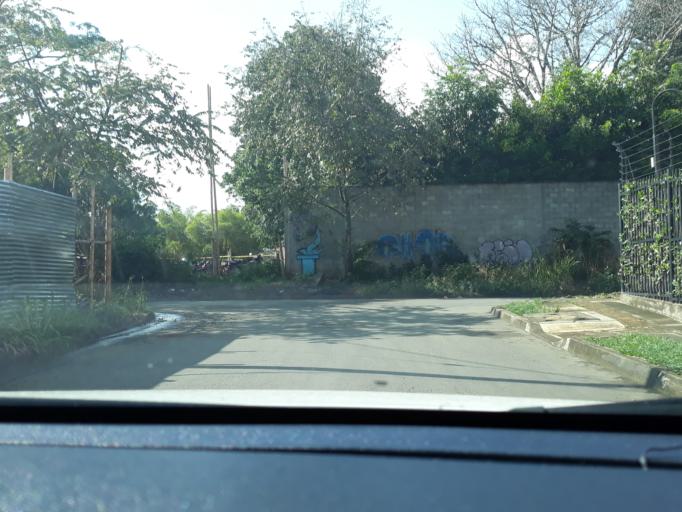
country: CO
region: Valle del Cauca
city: Cali
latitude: 3.3544
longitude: -76.5175
